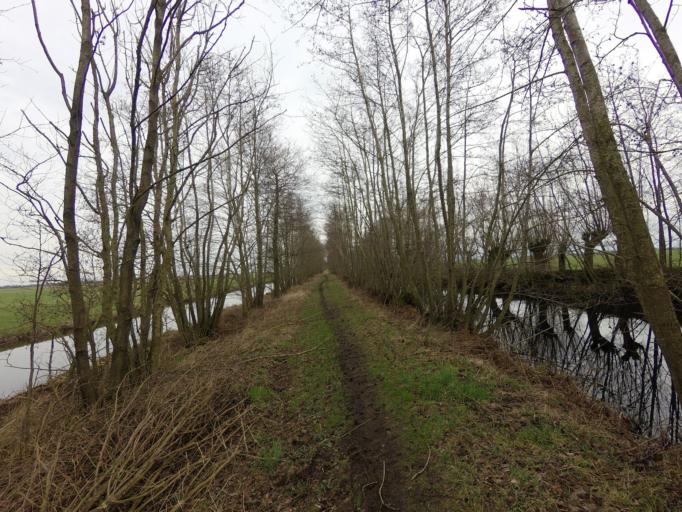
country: NL
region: Utrecht
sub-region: Gemeente Oudewater
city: Oudewater
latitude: 51.9926
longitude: 4.8561
